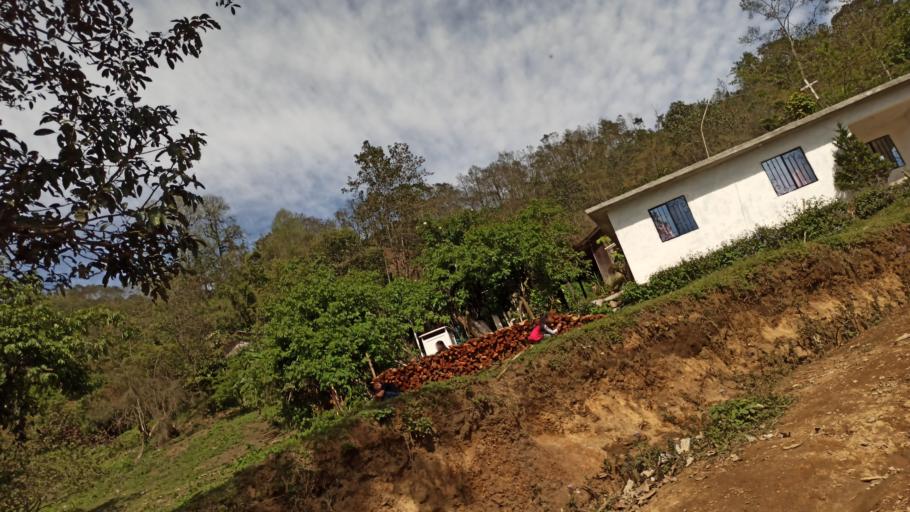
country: MX
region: Veracruz
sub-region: La Perla
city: Metlac Hernandez (Metlac Primero)
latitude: 18.9696
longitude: -97.1025
